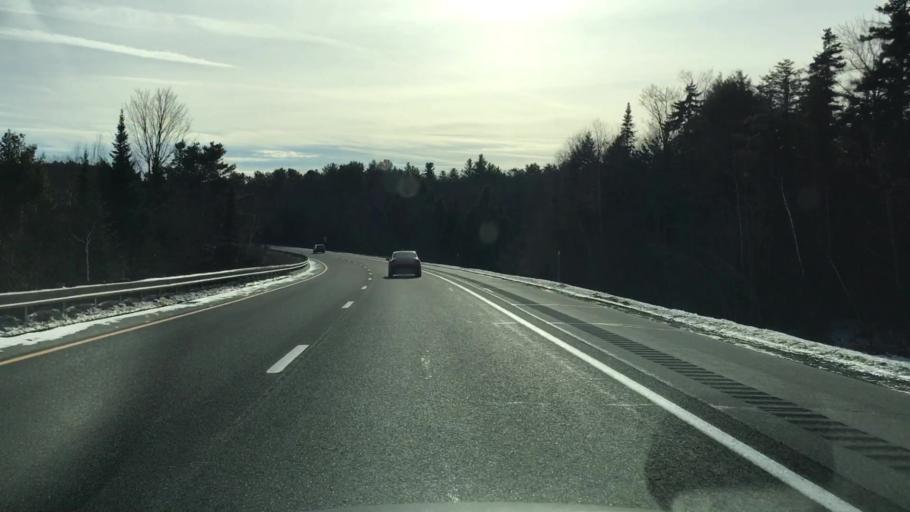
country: US
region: New Hampshire
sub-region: Sullivan County
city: Grantham
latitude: 43.5253
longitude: -72.1421
